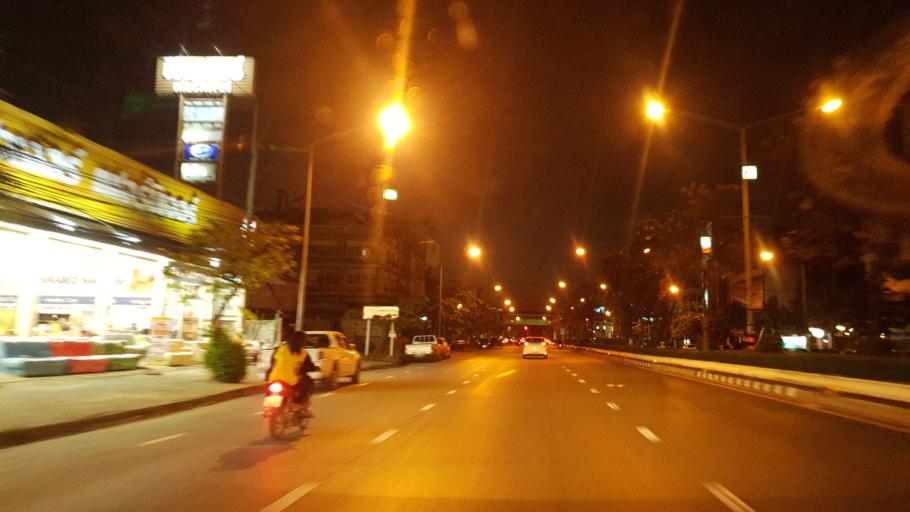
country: TH
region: Phitsanulok
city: Phitsanulok
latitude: 16.8146
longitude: 100.2767
